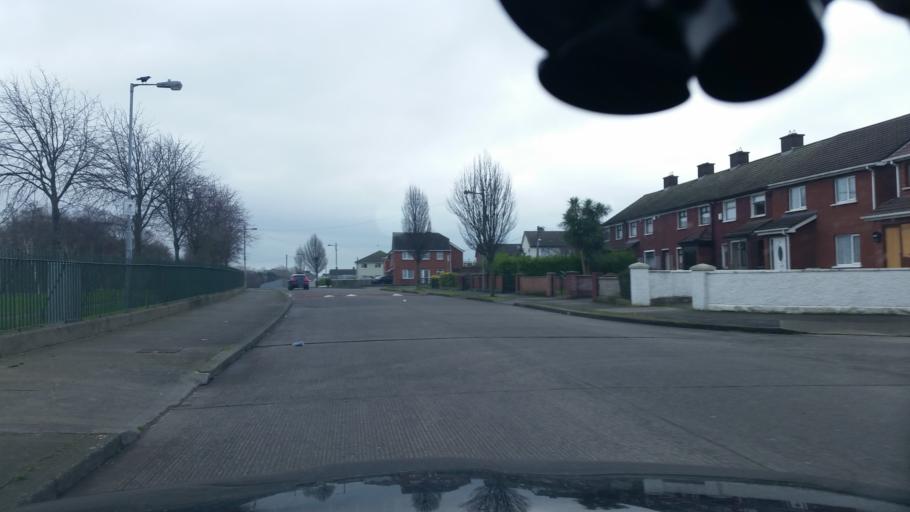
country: IE
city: Bonnybrook
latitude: 53.3964
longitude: -6.2084
